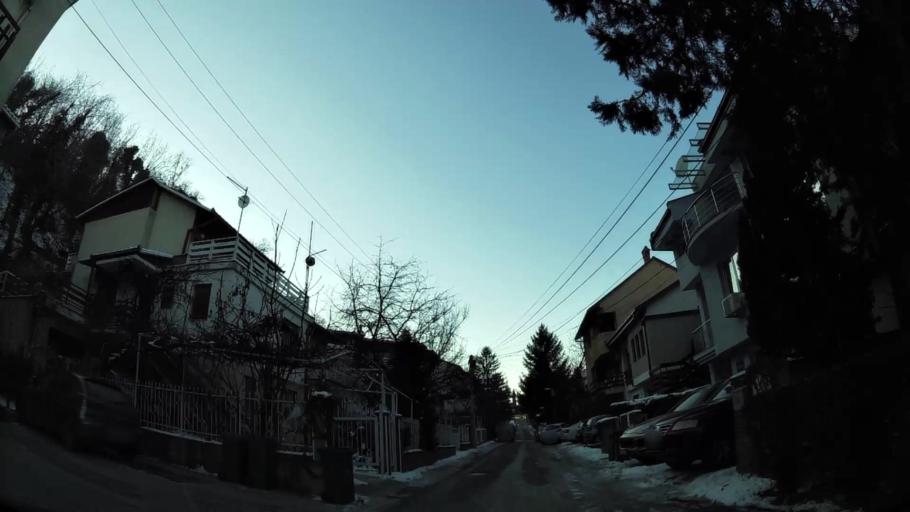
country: MK
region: Karpos
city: Skopje
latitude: 41.9916
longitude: 21.4023
